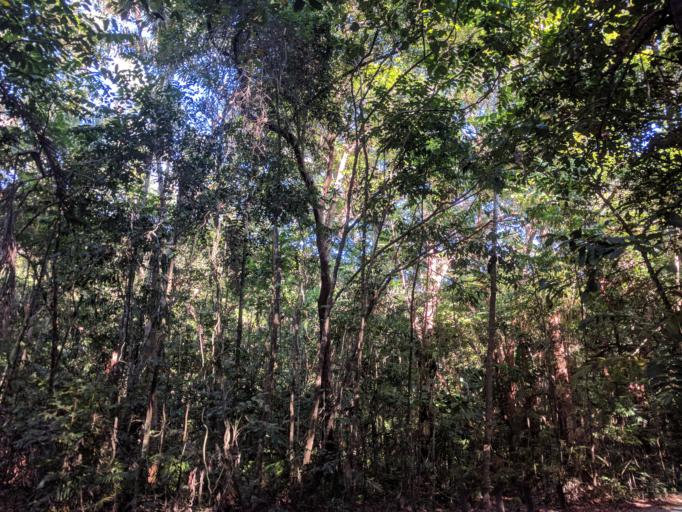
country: AU
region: Queensland
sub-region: Cairns
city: Port Douglas
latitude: -16.1351
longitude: 145.4518
